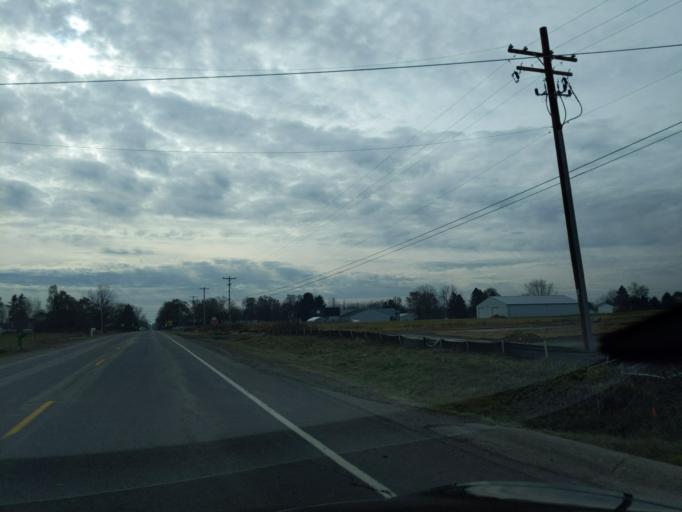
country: US
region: Michigan
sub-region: Ingham County
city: Holt
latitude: 42.5849
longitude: -84.5229
